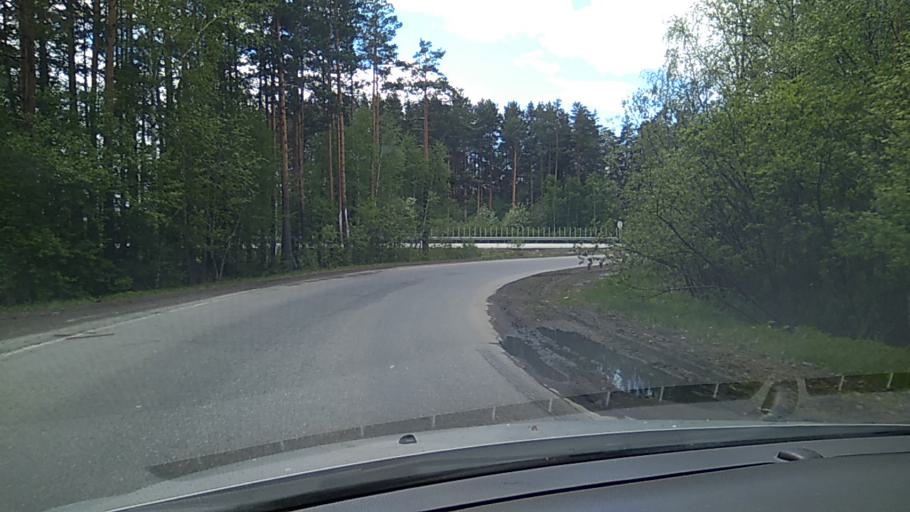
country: RU
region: Sverdlovsk
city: Istok
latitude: 56.8036
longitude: 60.7930
